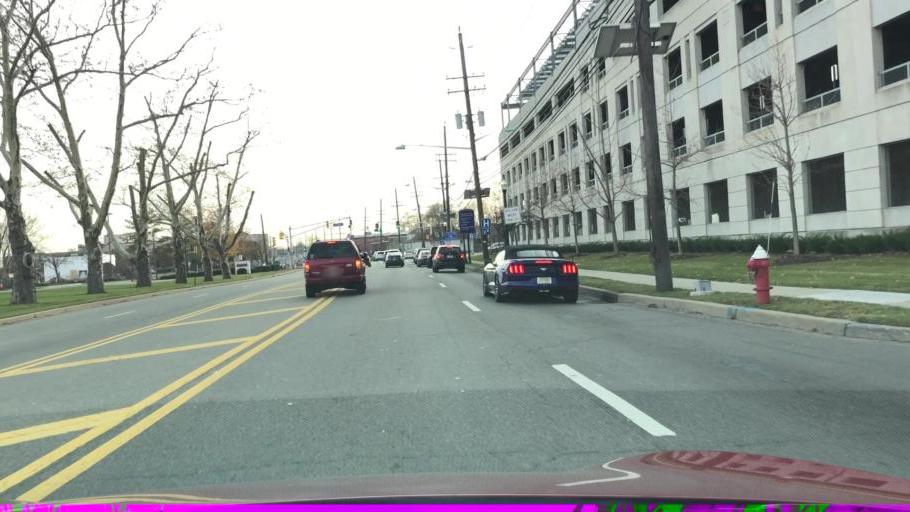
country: US
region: New Jersey
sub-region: Bergen County
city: Hackensack
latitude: 40.8775
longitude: -74.0412
